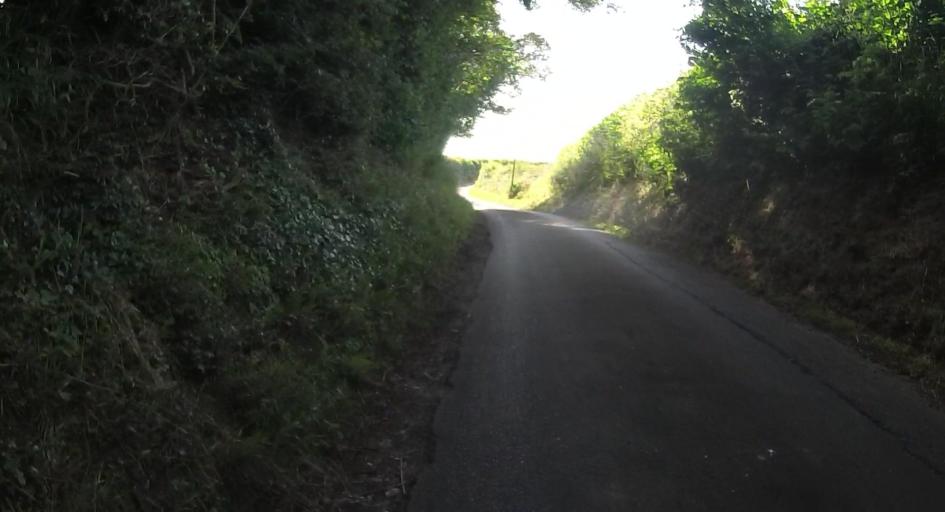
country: GB
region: England
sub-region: Hampshire
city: Long Sutton
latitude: 51.1821
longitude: -0.9257
